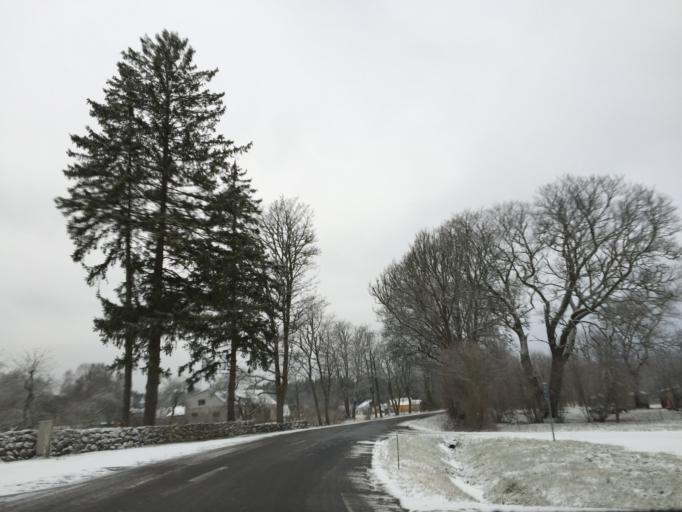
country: EE
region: Saare
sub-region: Orissaare vald
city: Orissaare
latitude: 58.6098
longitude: 23.3009
